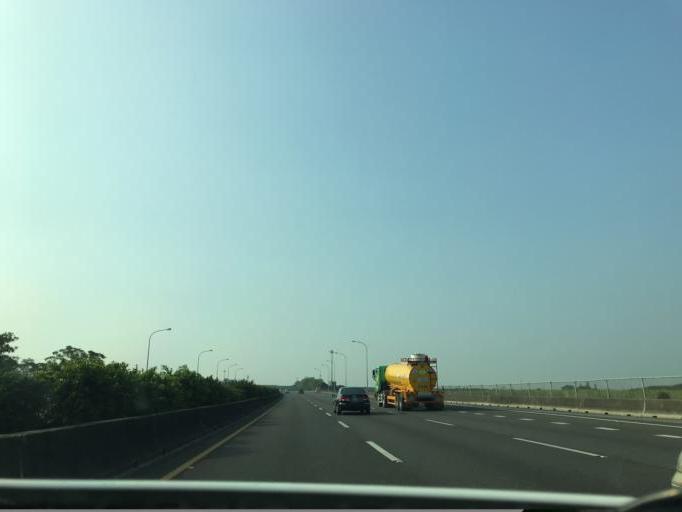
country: TW
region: Taiwan
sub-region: Chiayi
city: Taibao
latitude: 23.4334
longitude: 120.3599
